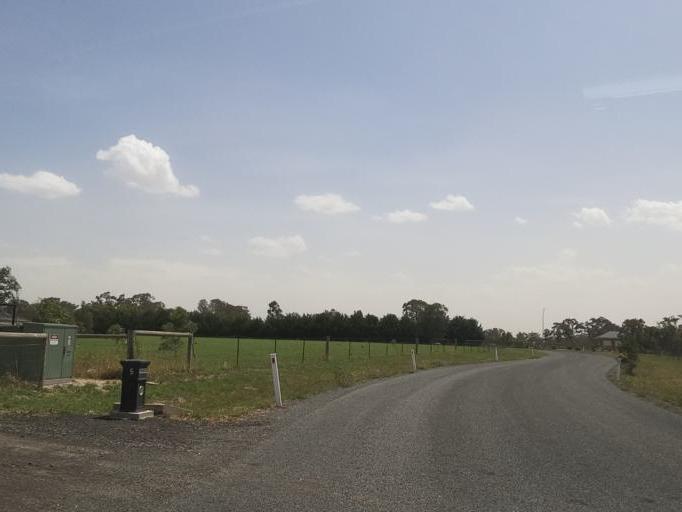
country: AU
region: Victoria
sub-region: Hume
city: Craigieburn
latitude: -37.5570
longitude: 144.8897
